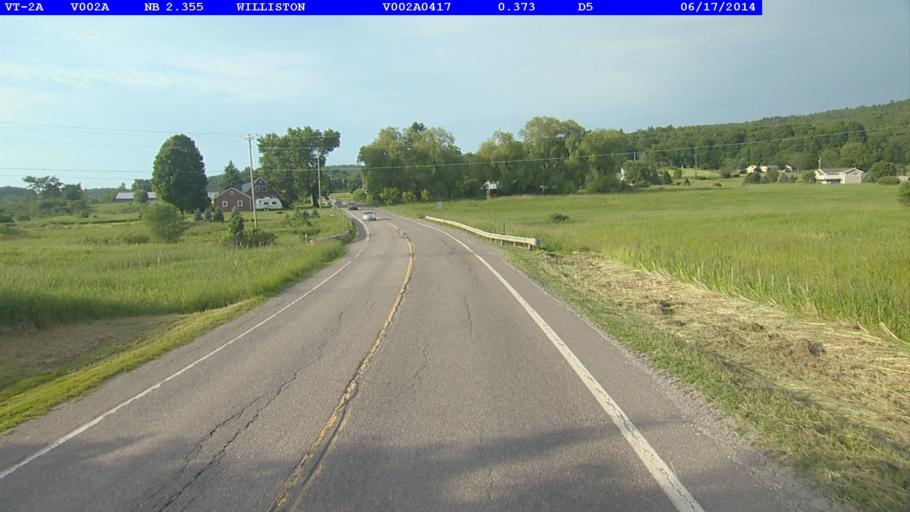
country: US
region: Vermont
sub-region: Chittenden County
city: Williston
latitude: 44.4032
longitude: -73.1261
